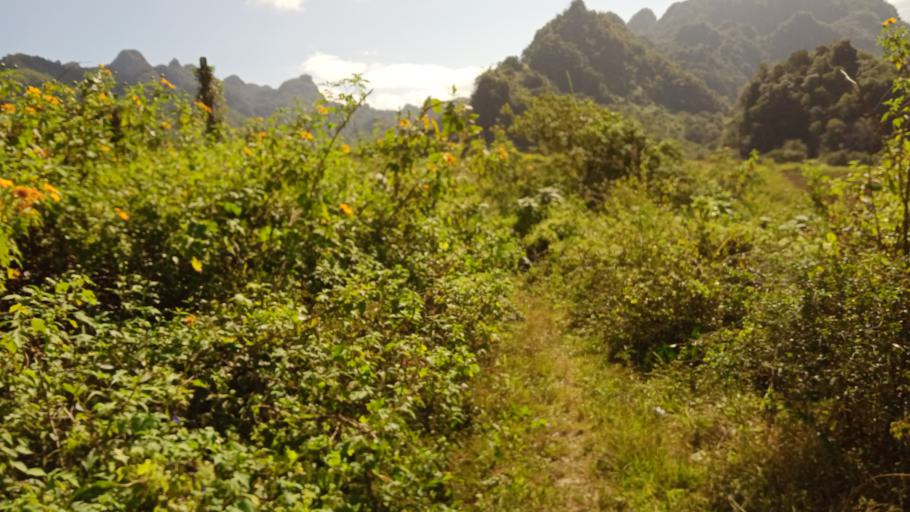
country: LA
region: Xiangkhoang
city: Phonsavan
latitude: 19.1038
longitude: 102.9316
